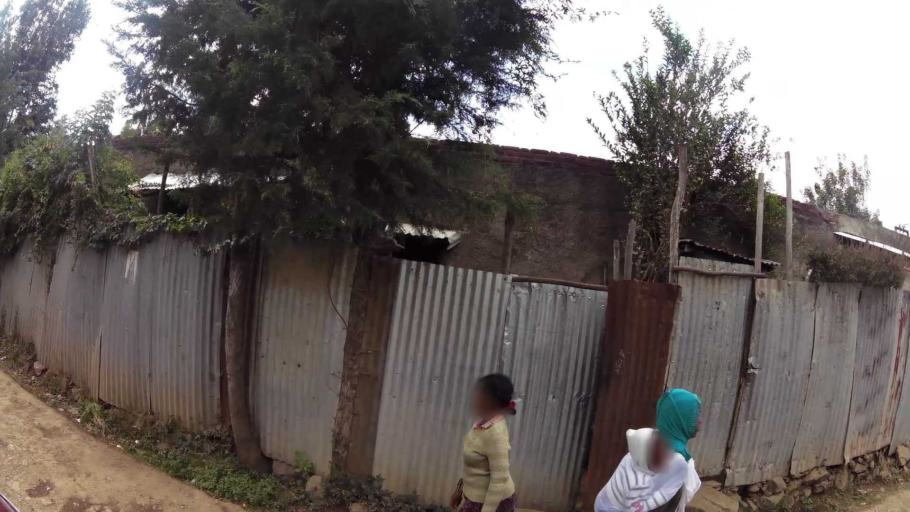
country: ET
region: Adis Abeba
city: Addis Ababa
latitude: 8.9470
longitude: 38.7538
